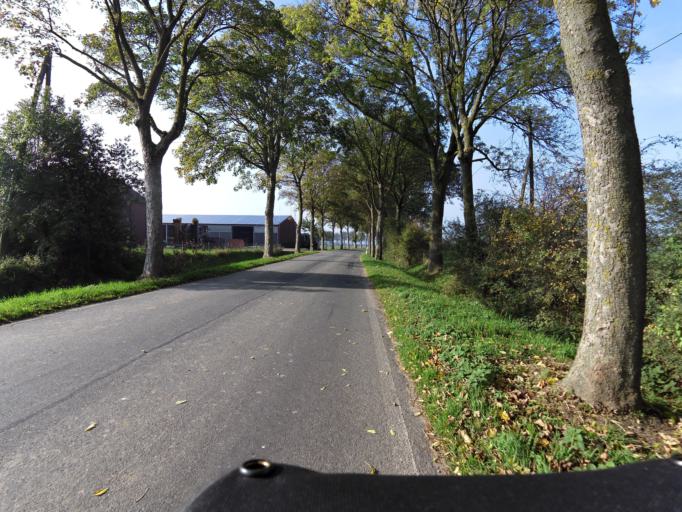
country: DE
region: North Rhine-Westphalia
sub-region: Regierungsbezirk Dusseldorf
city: Kranenburg
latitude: 51.8262
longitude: 6.0047
